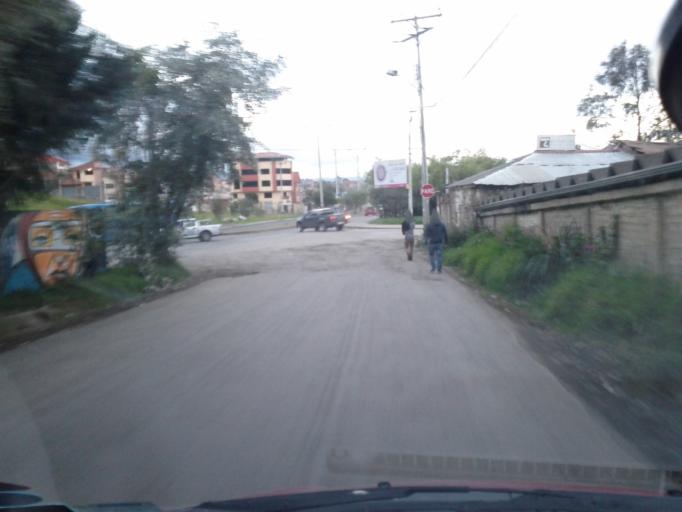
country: EC
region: Azuay
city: Cuenca
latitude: -2.9191
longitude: -79.0240
